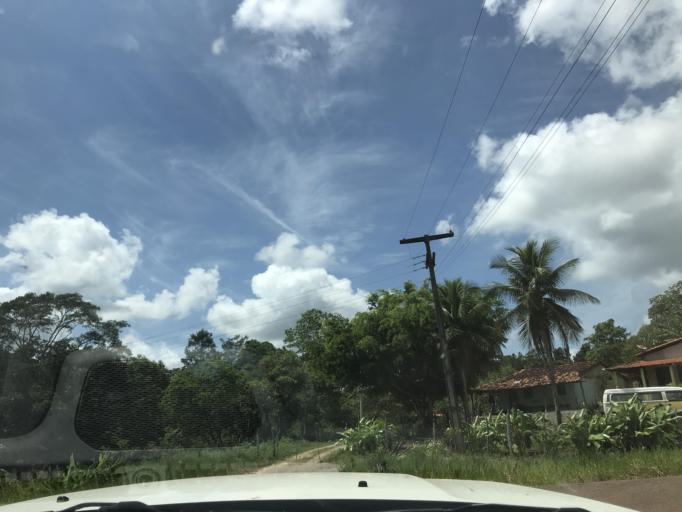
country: BR
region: Bahia
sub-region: Entre Rios
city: Entre Rios
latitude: -12.2419
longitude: -38.0963
